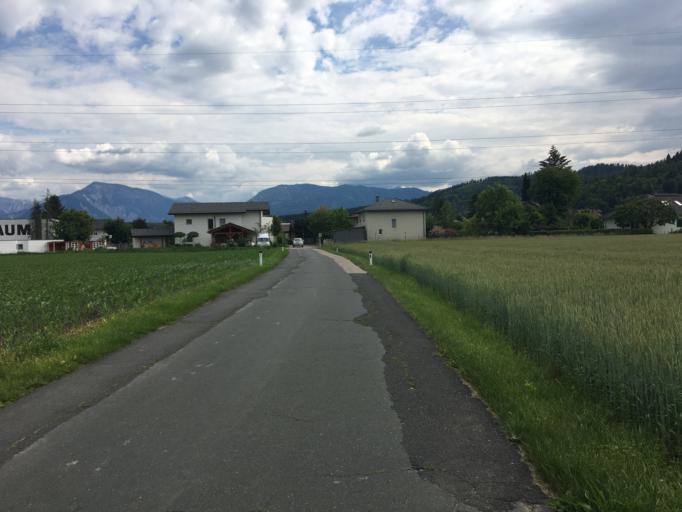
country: AT
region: Carinthia
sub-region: Klagenfurt am Woerthersee
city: Klagenfurt am Woerthersee
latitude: 46.6011
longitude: 14.2724
